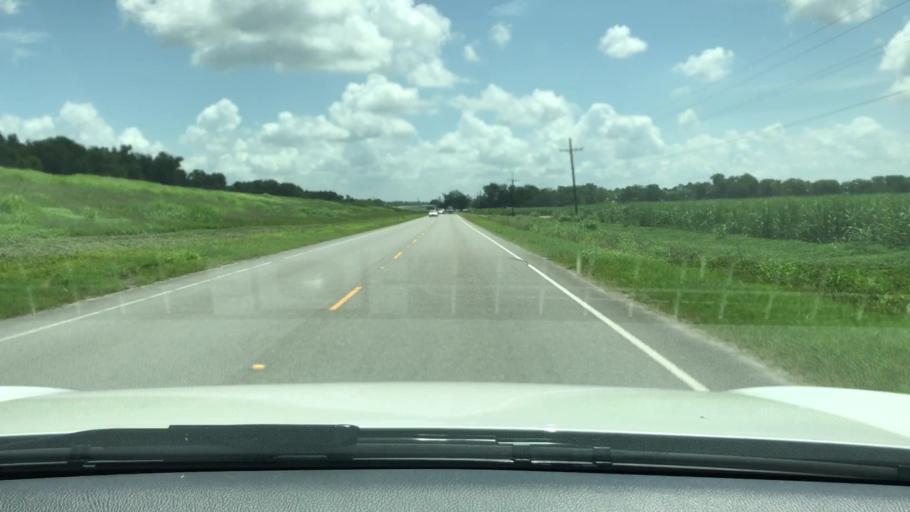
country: US
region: Louisiana
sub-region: Iberville Parish
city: Plaquemine
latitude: 30.2729
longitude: -91.1955
